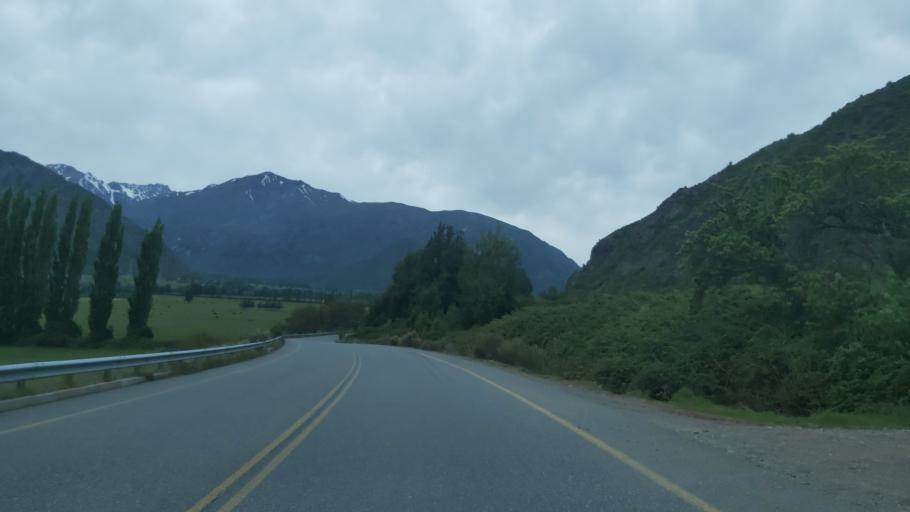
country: CL
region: Maule
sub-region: Provincia de Linares
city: Colbun
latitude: -35.8124
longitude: -70.8703
